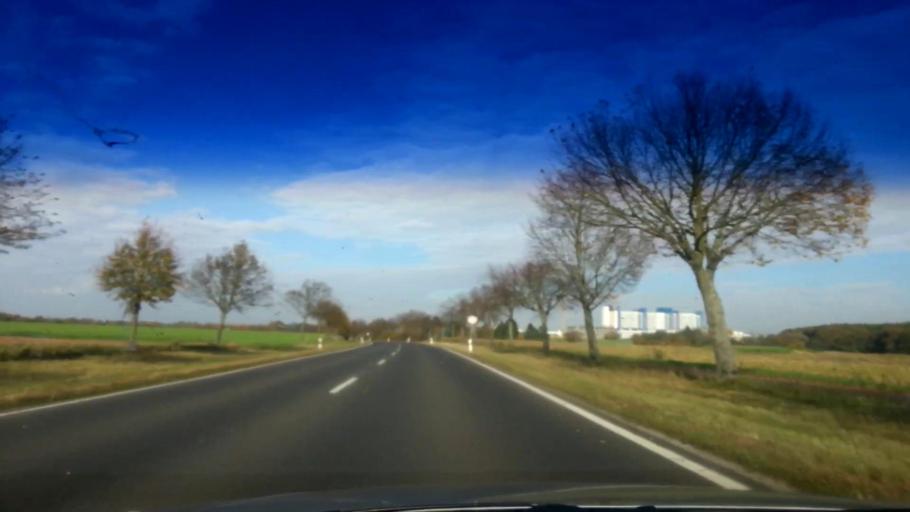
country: DE
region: Bavaria
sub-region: Upper Franconia
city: Stegaurach
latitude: 49.8610
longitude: 10.8807
